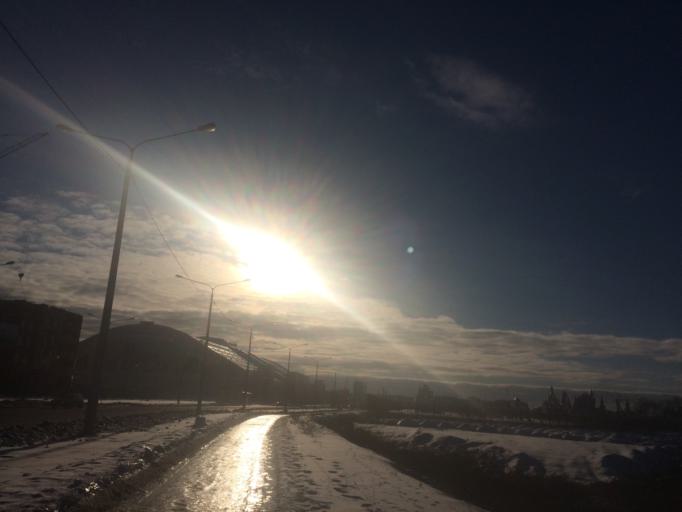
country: RU
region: Mariy-El
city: Yoshkar-Ola
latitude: 56.6432
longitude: 47.9165
